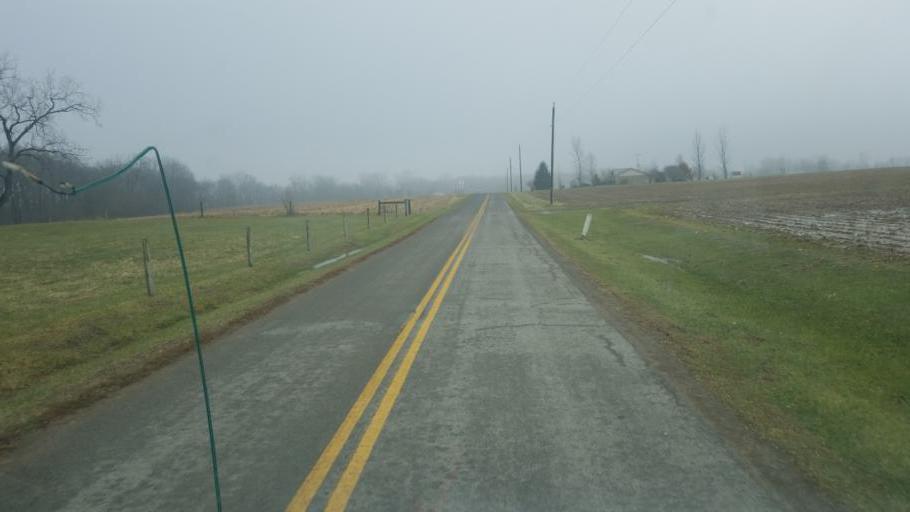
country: US
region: Ohio
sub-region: Hardin County
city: Kenton
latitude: 40.5031
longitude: -83.5269
